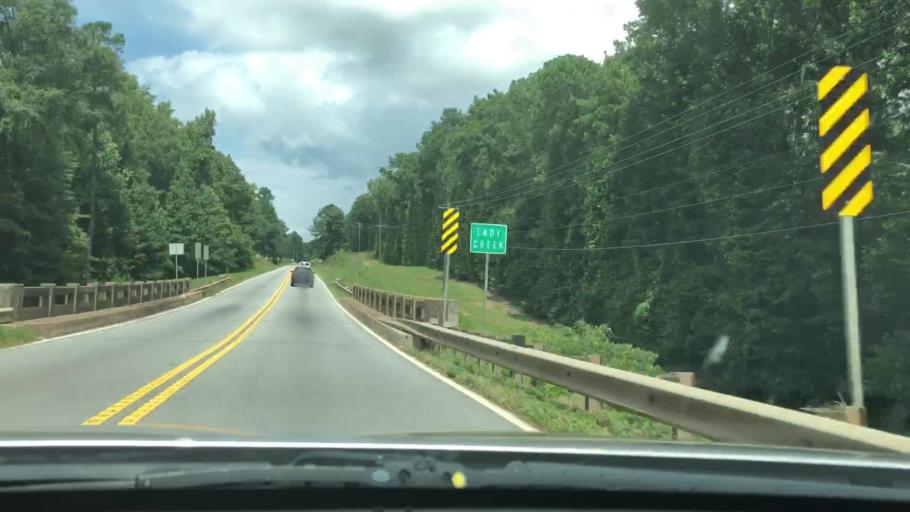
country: US
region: Georgia
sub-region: Lamar County
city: Barnesville
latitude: 33.1441
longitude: -84.1459
